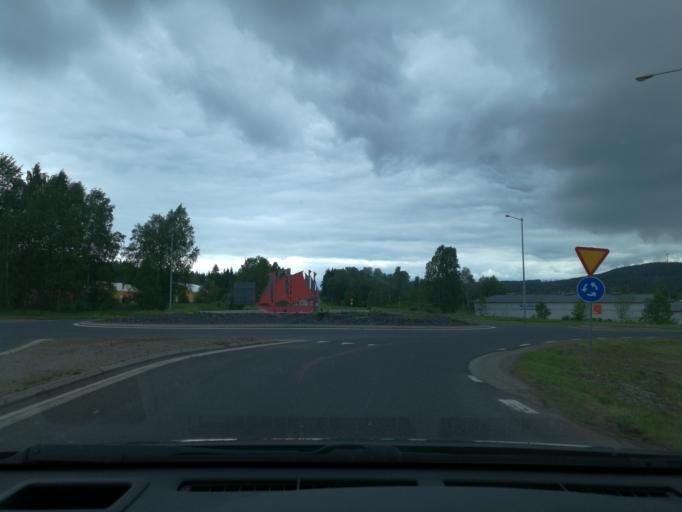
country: SE
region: Dalarna
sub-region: Smedjebackens Kommun
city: Smedjebacken
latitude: 60.1319
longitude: 15.4007
